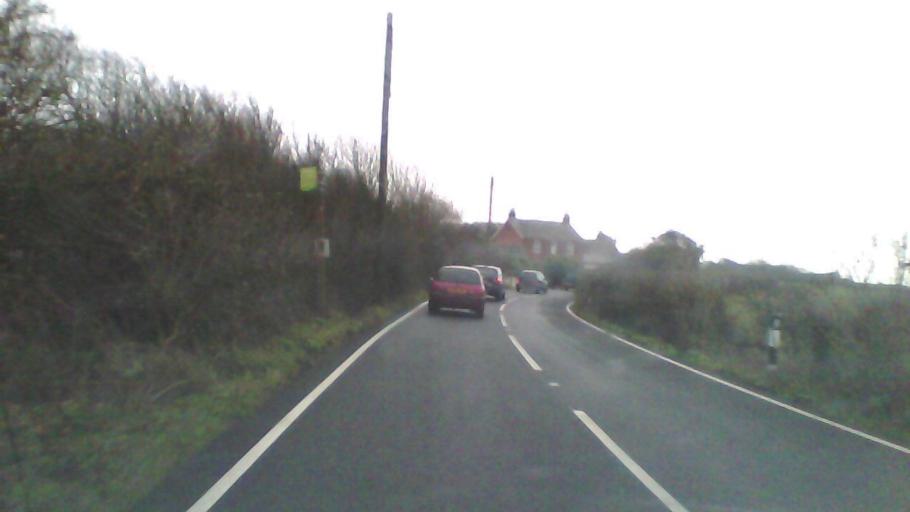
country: GB
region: England
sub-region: Isle of Wight
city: Newport
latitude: 50.6897
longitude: -1.2487
